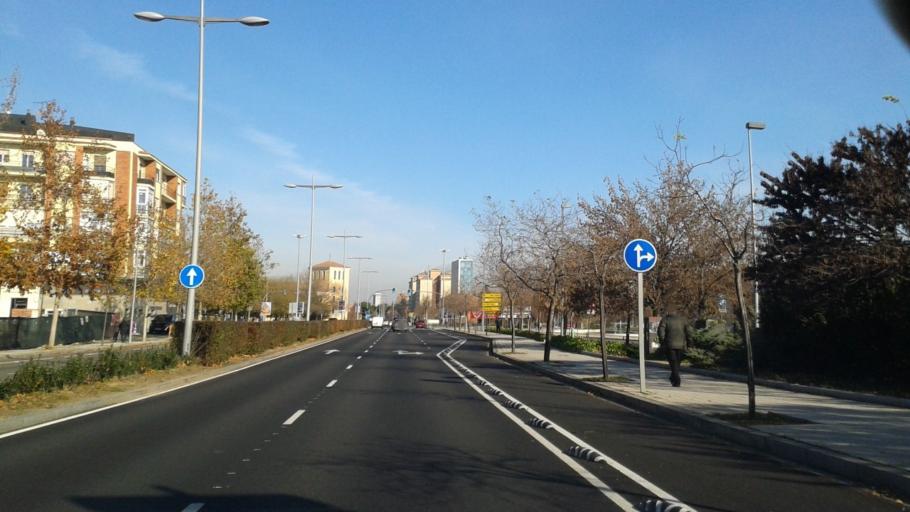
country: ES
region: Castille and Leon
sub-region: Provincia de Valladolid
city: Valladolid
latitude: 41.6377
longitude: -4.7465
